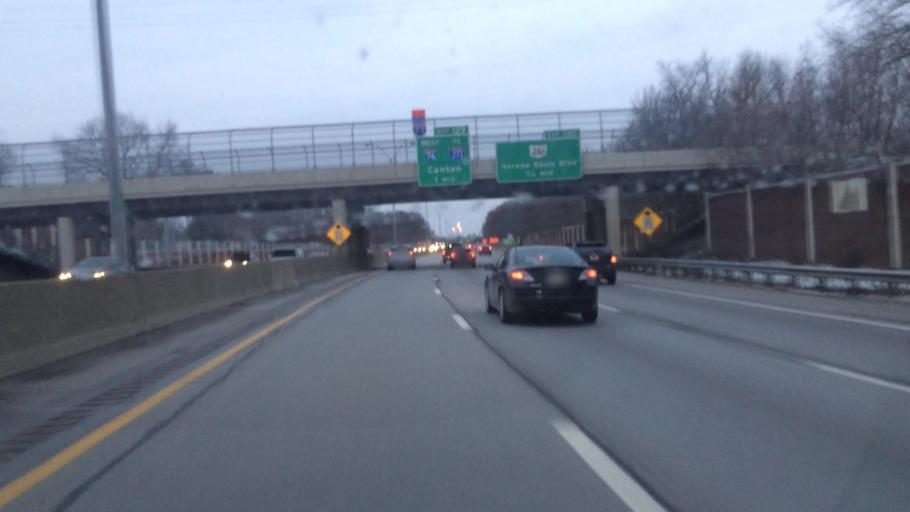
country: US
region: Ohio
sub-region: Summit County
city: Akron
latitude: 41.0771
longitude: -81.5741
